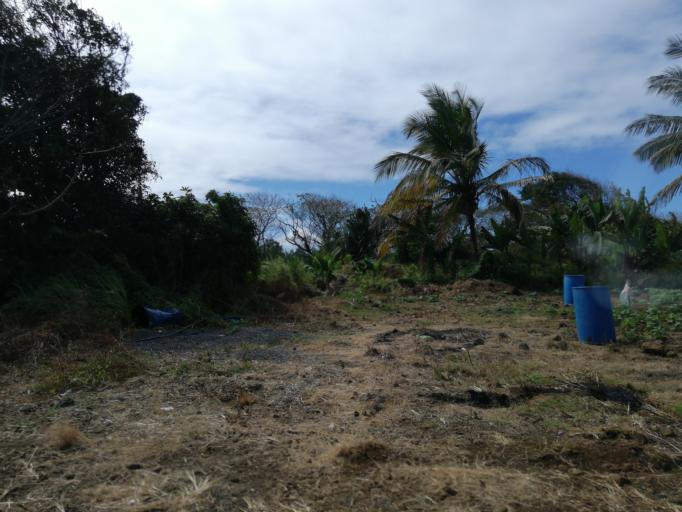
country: MU
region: Grand Port
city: Plaine Magnien
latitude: -20.4652
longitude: 57.6759
